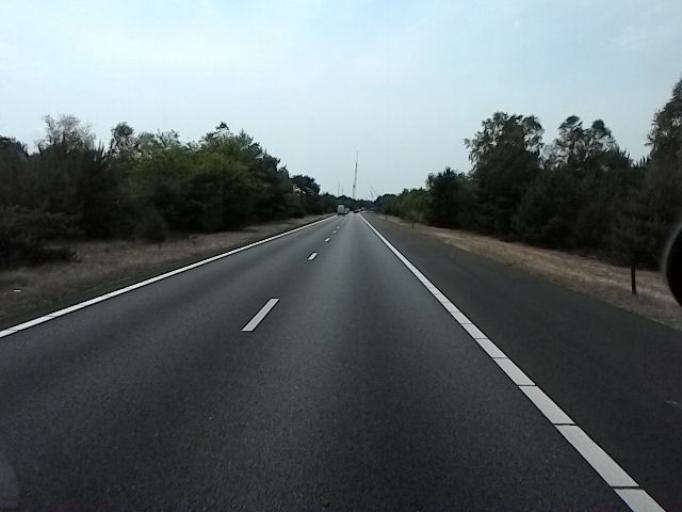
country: NL
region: Gelderland
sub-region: Gemeente Oldebroek
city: Oldebroek
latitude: 52.4178
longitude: 5.9083
